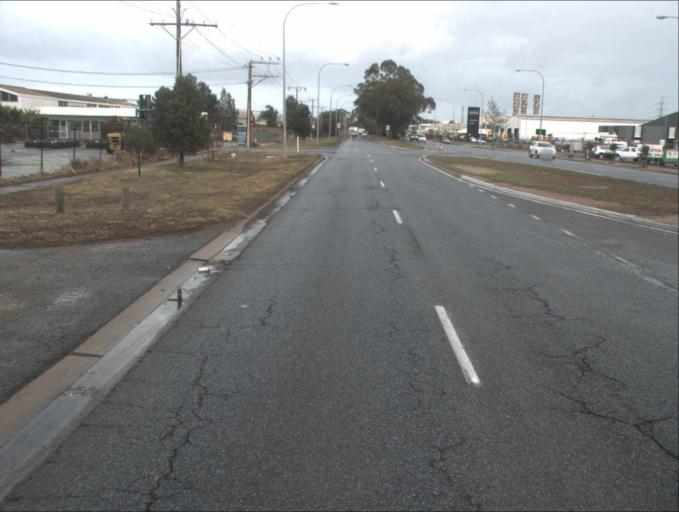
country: AU
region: South Australia
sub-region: Port Adelaide Enfield
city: Enfield
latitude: -34.8437
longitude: 138.5887
